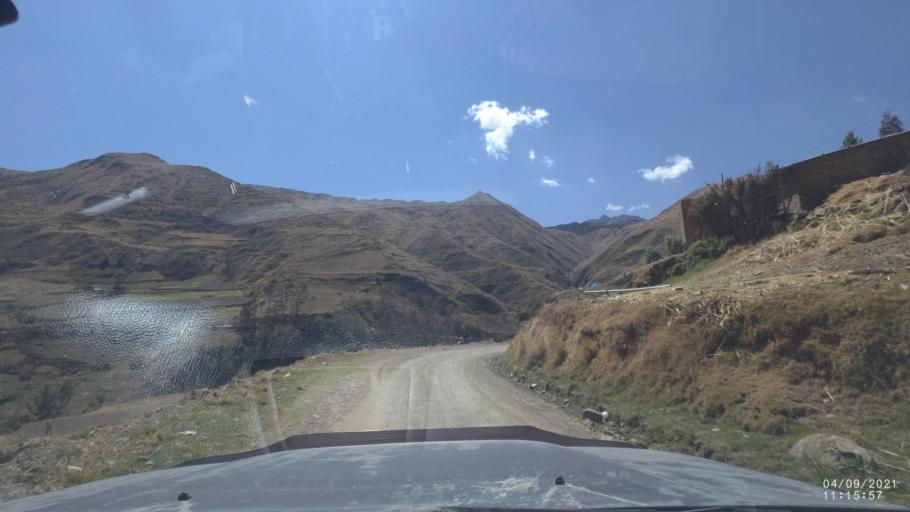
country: BO
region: Cochabamba
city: Sipe Sipe
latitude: -17.2717
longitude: -66.4877
